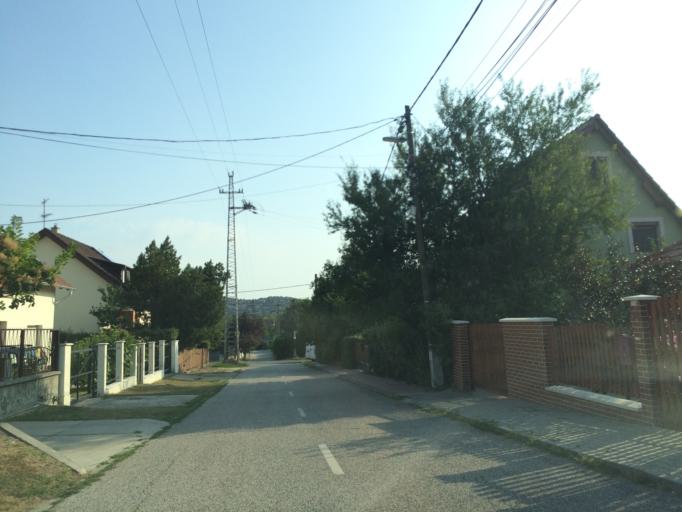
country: HU
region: Pest
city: Szentendre
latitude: 47.6758
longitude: 19.0533
